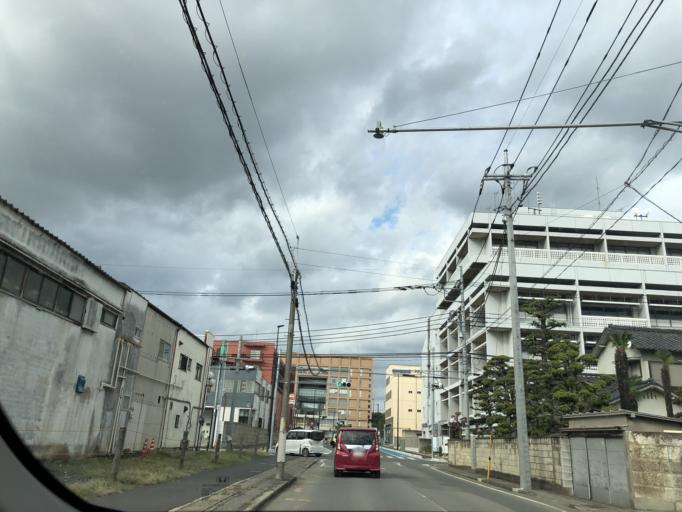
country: JP
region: Tochigi
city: Sano
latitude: 36.3119
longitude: 139.5784
